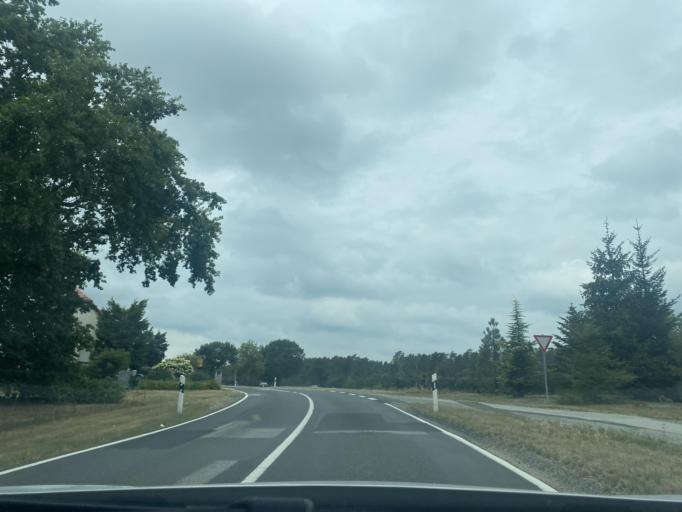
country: DE
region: Saxony
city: Mucka
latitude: 51.2829
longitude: 14.6665
